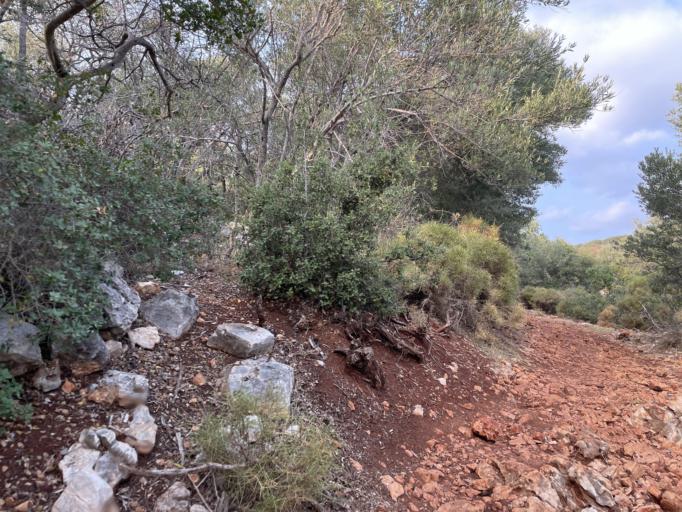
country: TR
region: Antalya
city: Kas
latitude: 36.1629
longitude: 29.6546
